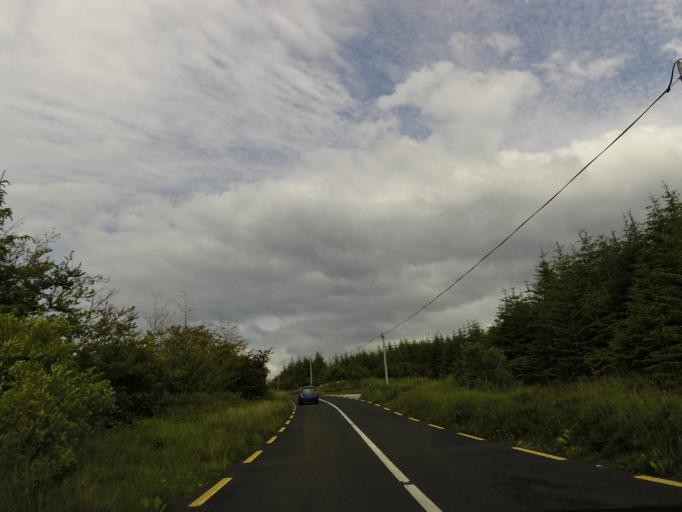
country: IE
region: Connaught
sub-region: County Galway
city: Bearna
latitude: 53.0575
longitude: -9.2084
